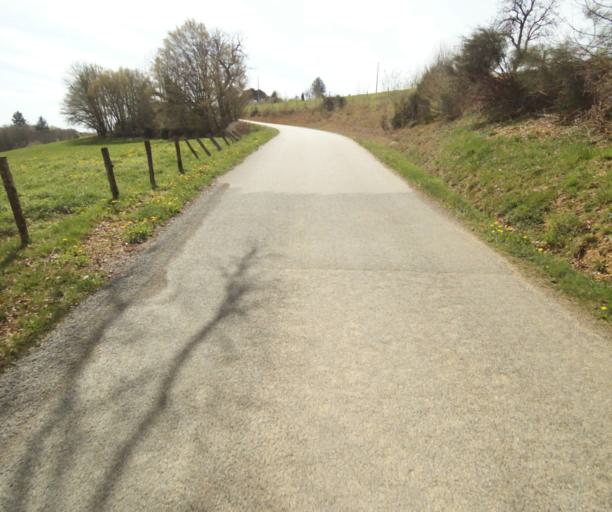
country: FR
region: Limousin
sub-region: Departement de la Correze
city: Naves
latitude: 45.3616
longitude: 1.7975
